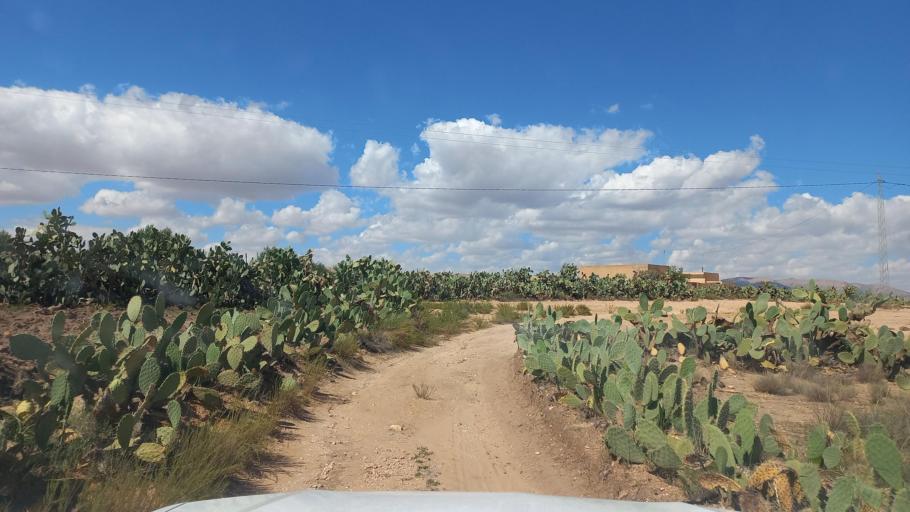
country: TN
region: Al Qasrayn
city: Sbiba
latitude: 35.3547
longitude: 9.0139
